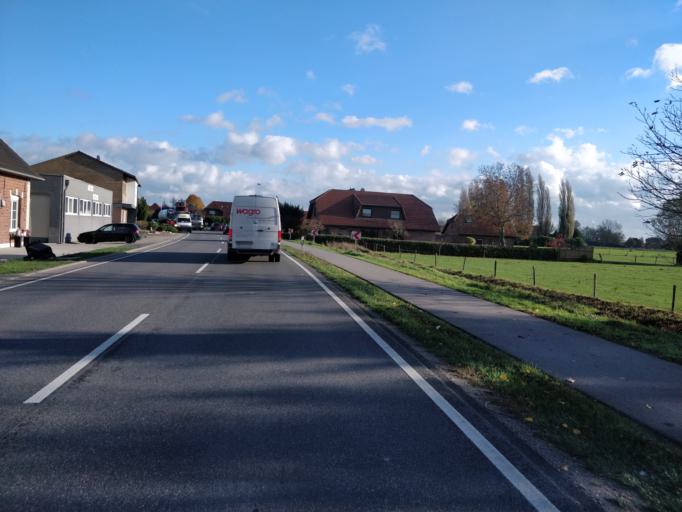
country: NL
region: Gelderland
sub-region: Oude IJsselstreek
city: Gendringen
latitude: 51.8247
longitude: 6.3262
